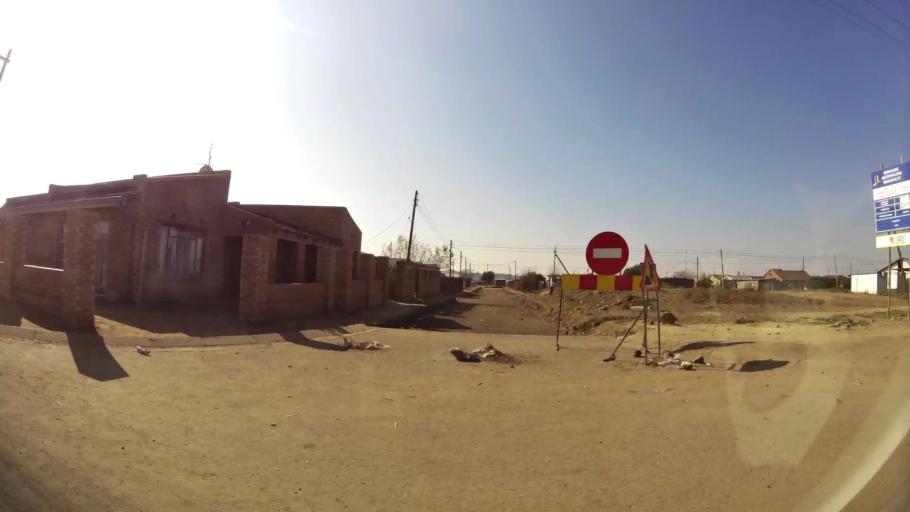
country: ZA
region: Orange Free State
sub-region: Mangaung Metropolitan Municipality
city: Bloemfontein
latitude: -29.1903
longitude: 26.2472
